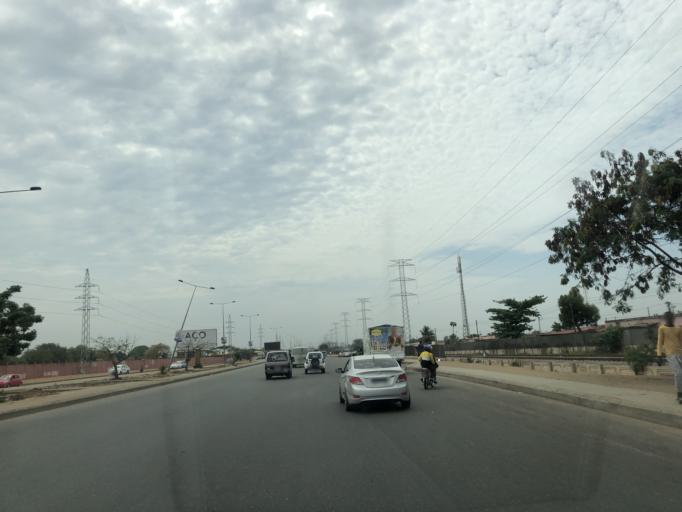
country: AO
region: Luanda
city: Luanda
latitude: -8.8622
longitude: 13.3065
